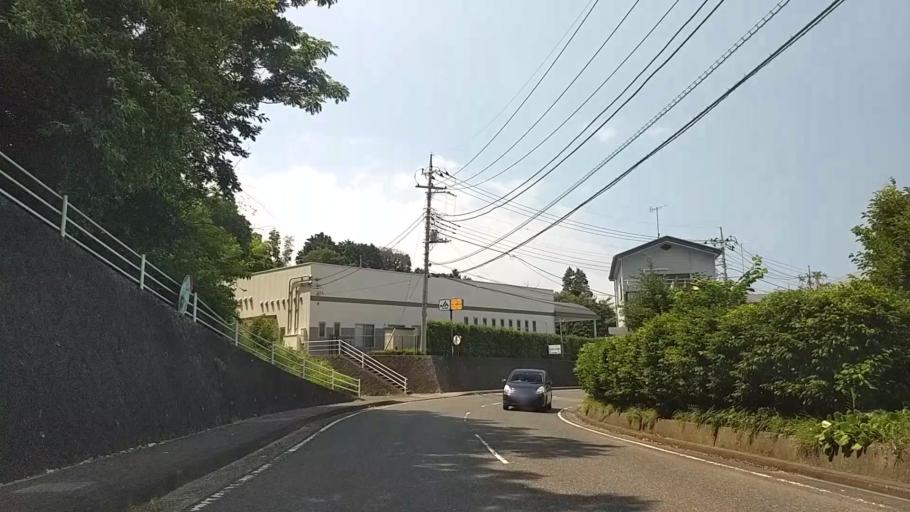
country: JP
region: Shizuoka
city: Ito
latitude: 34.9431
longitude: 139.1137
